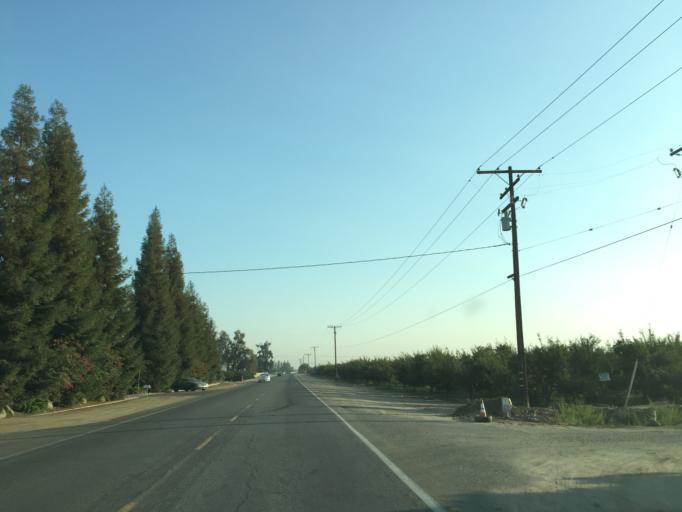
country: US
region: California
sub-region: Tulare County
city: Visalia
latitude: 36.3817
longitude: -119.2788
